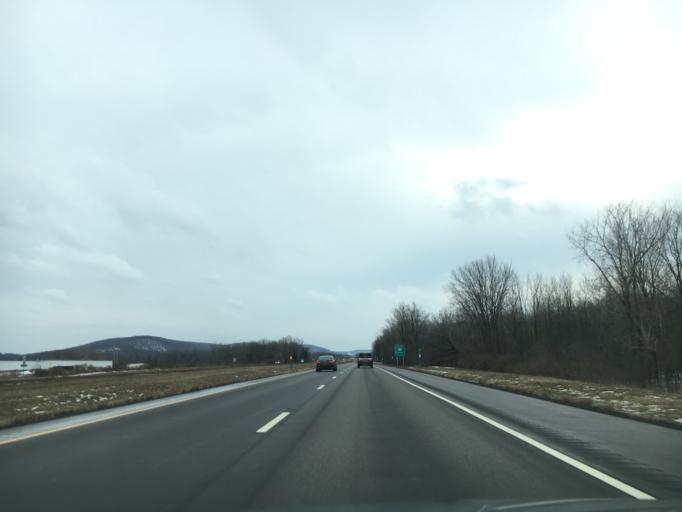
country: US
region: New York
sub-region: Cortland County
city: Homer
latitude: 42.7575
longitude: -76.1348
